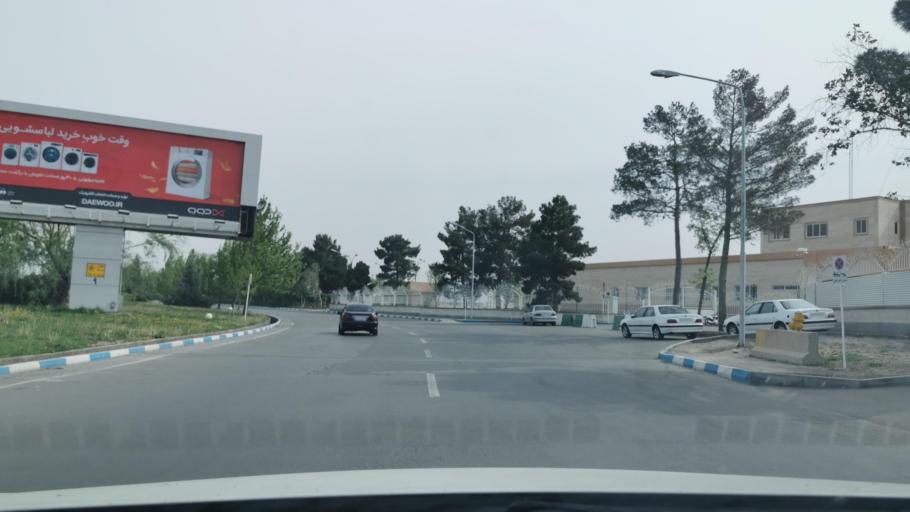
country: IR
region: Razavi Khorasan
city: Mashhad
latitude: 36.2327
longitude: 59.6340
